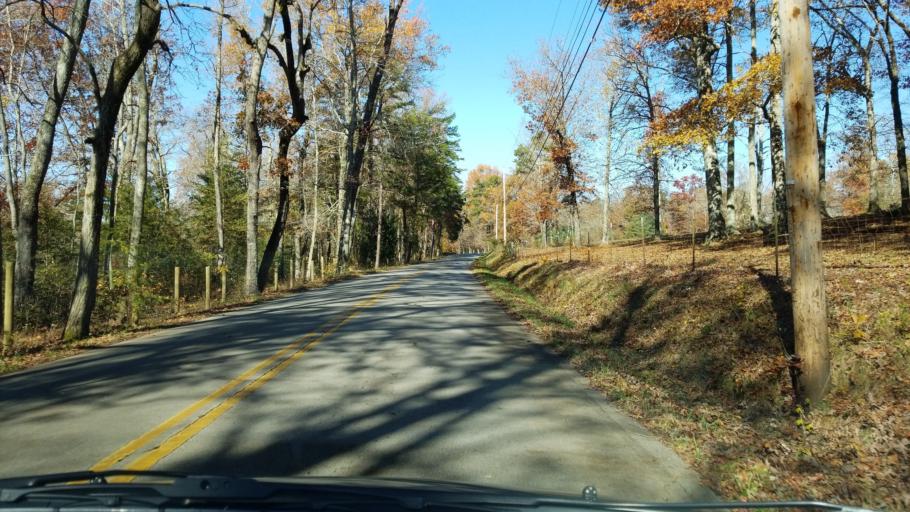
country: US
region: Tennessee
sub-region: Hamilton County
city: Falling Water
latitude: 35.2194
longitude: -85.2763
